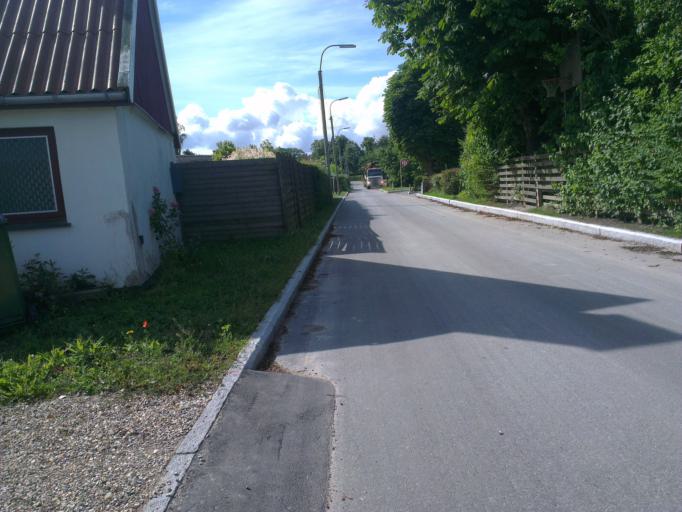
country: DK
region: Capital Region
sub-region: Frederikssund Kommune
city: Jaegerspris
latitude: 55.8592
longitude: 11.9966
